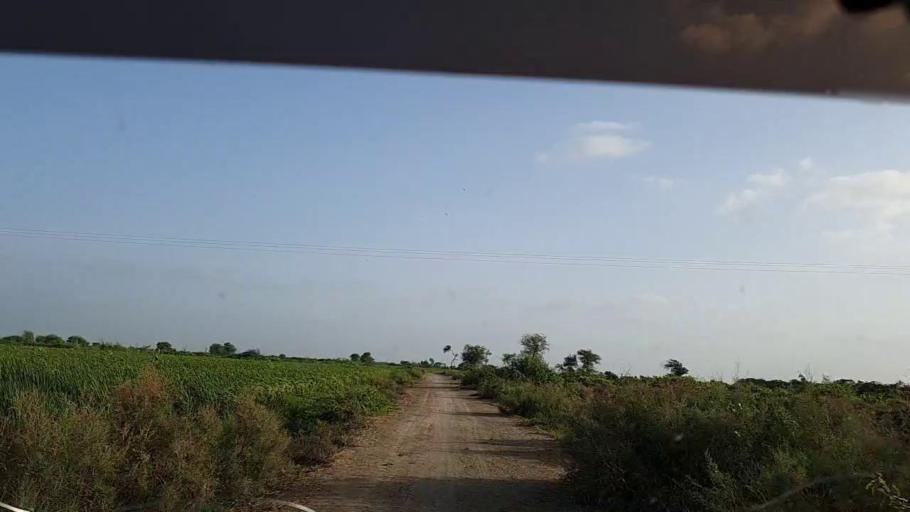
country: PK
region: Sindh
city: Badin
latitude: 24.5529
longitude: 68.8635
